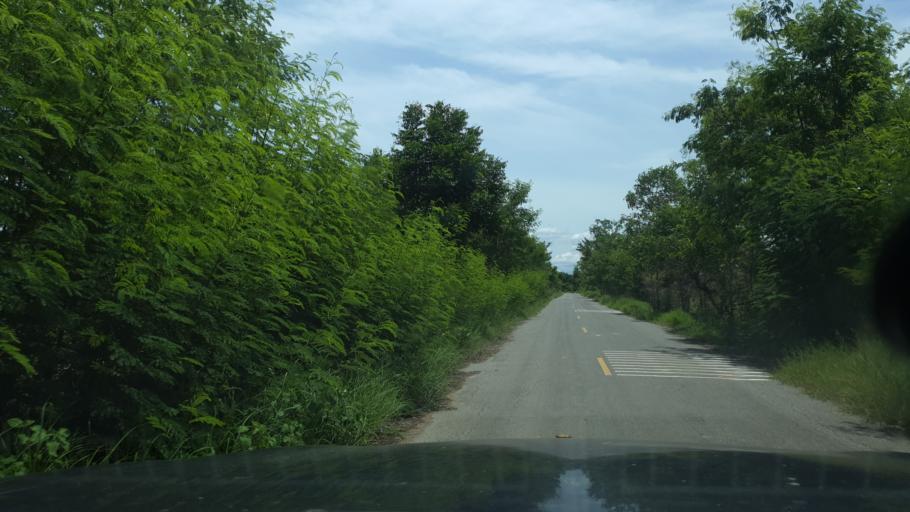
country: TH
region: Sukhothai
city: Ban Na
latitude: 17.0949
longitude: 99.6796
